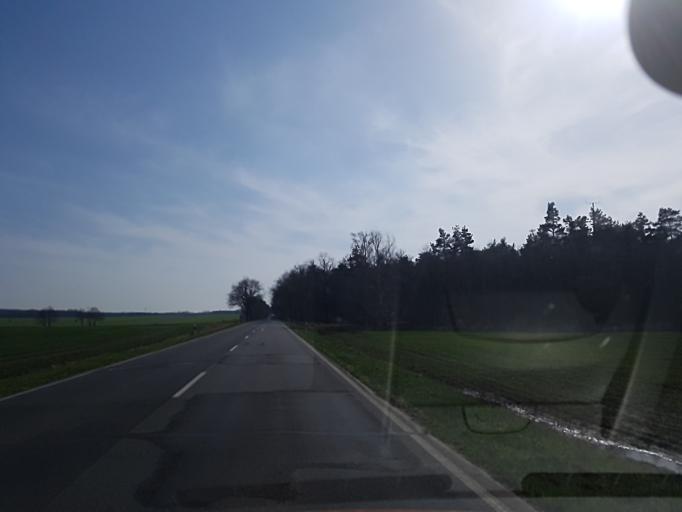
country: DE
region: Brandenburg
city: Calau
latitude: 51.7401
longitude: 13.9391
